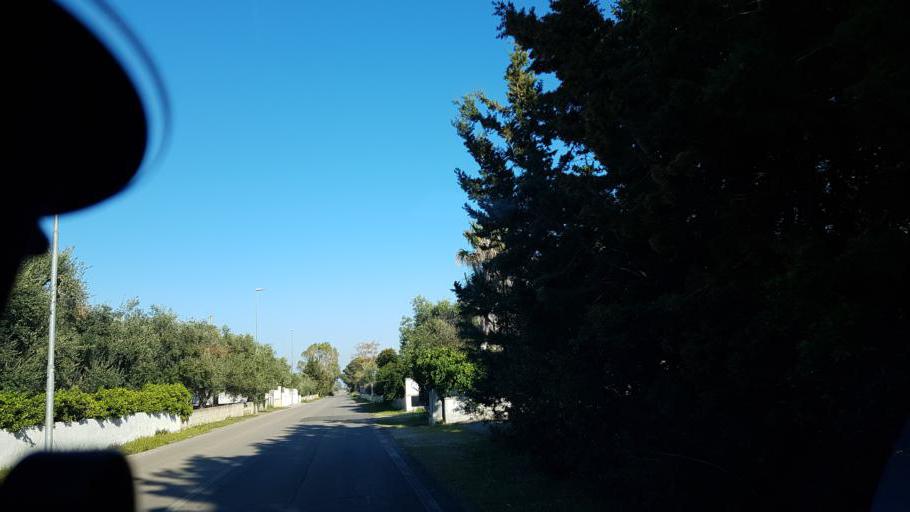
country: IT
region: Apulia
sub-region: Provincia di Lecce
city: Giorgilorio
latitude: 40.4564
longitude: 18.1984
